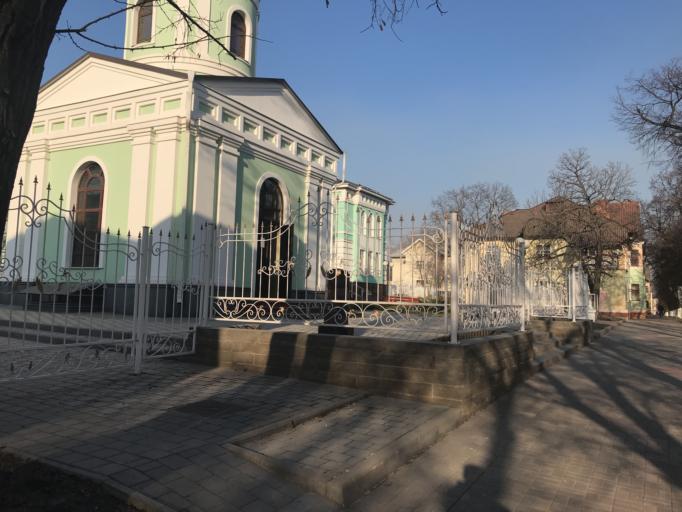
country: RU
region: Belgorod
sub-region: Belgorodskiy Rayon
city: Belgorod
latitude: 50.5965
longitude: 36.5804
